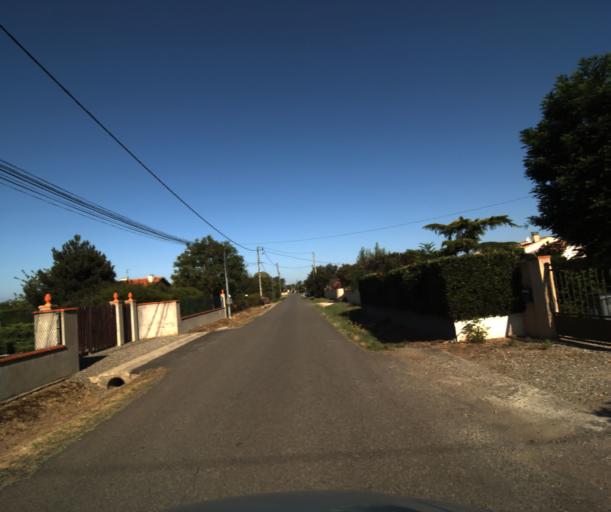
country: FR
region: Midi-Pyrenees
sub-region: Departement de la Haute-Garonne
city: Eaunes
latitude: 43.4349
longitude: 1.3670
